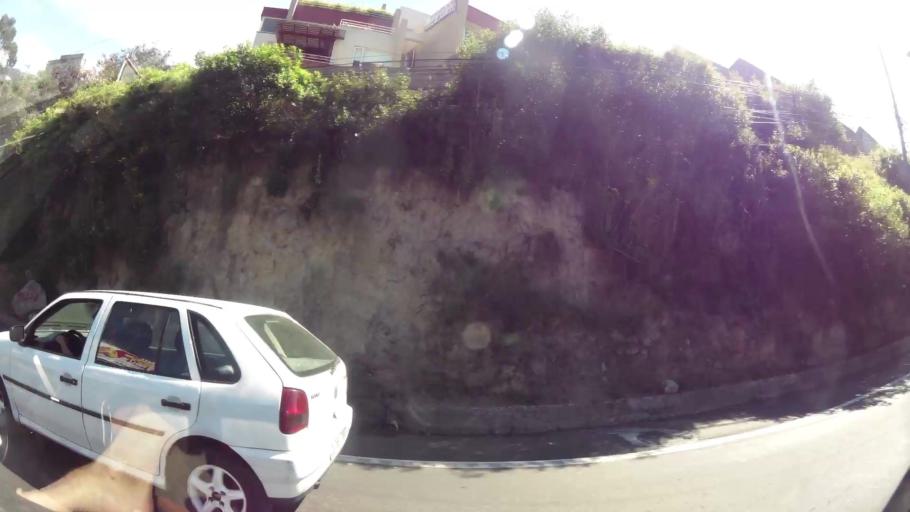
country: EC
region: Pichincha
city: Quito
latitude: -0.1937
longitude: -78.4438
